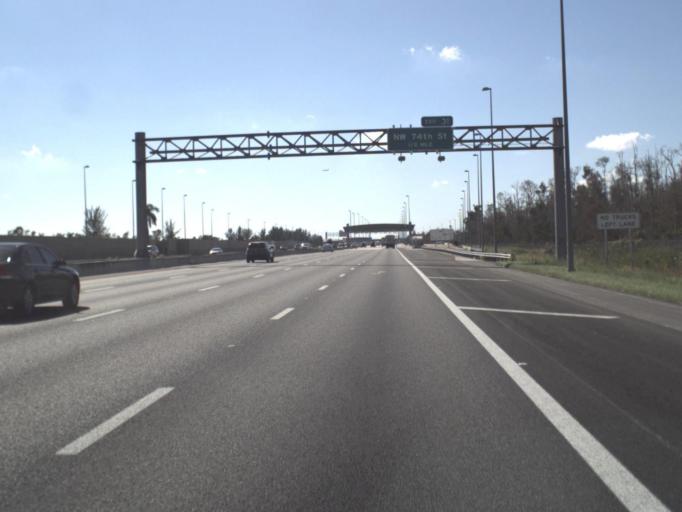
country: US
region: Florida
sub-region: Miami-Dade County
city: Doral
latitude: 25.8549
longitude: -80.3877
